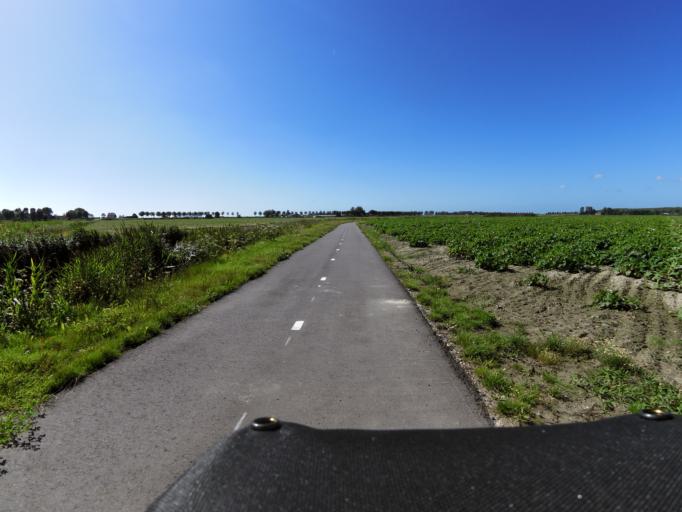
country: NL
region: South Holland
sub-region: Gemeente Goeree-Overflakkee
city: Dirksland
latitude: 51.7505
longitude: 4.0743
